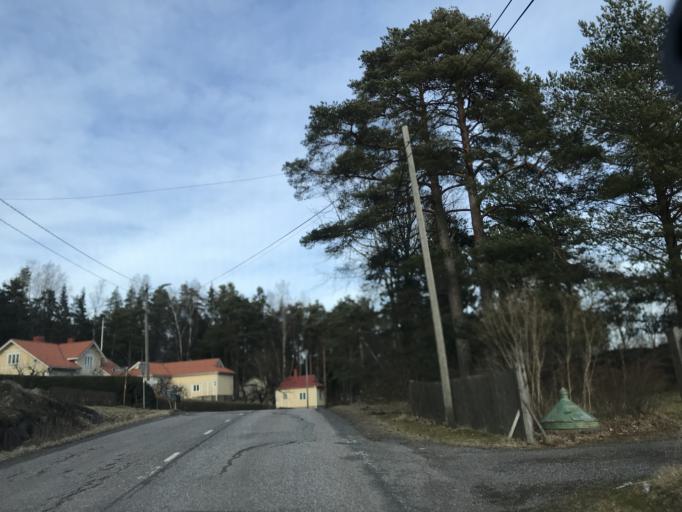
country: FI
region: Uusimaa
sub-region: Raaseporin
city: Pohja
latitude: 60.0974
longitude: 23.5360
